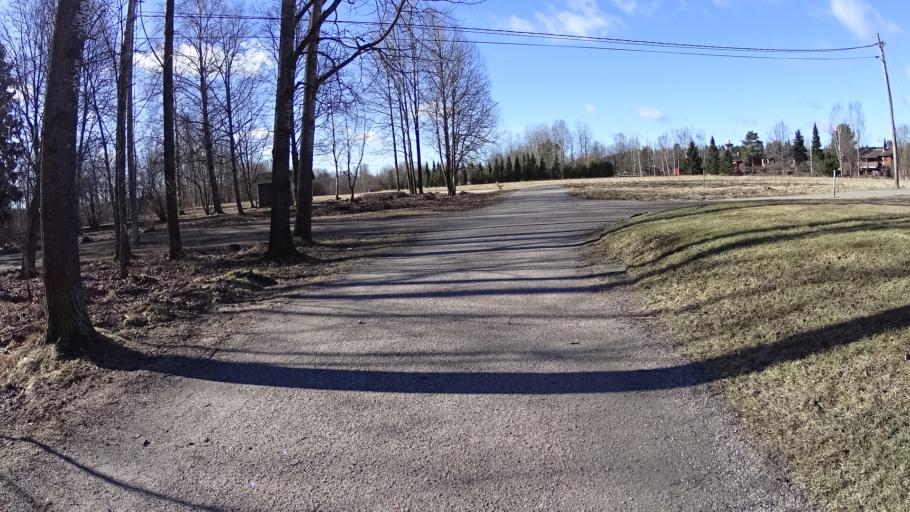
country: FI
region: Uusimaa
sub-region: Helsinki
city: Teekkarikylae
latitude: 60.2769
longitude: 24.8828
